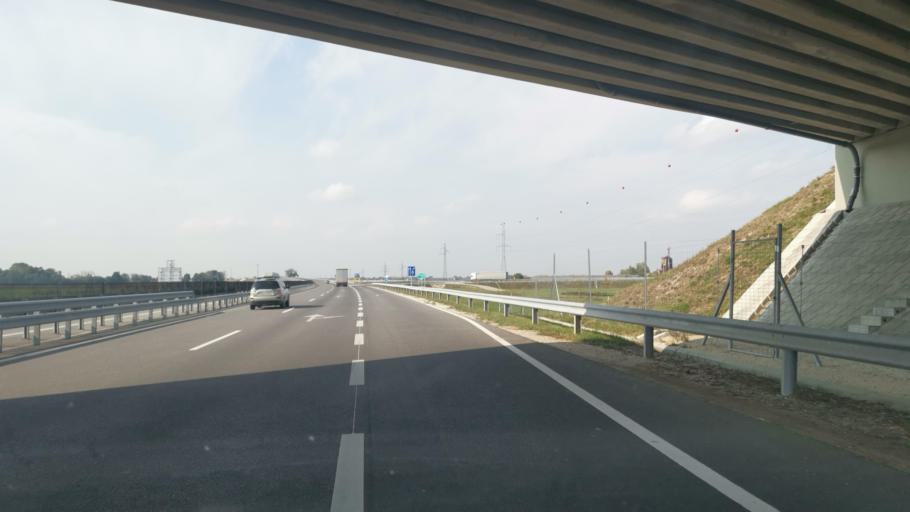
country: HU
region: Gyor-Moson-Sopron
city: Kapuvar
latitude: 47.5689
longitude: 17.0500
